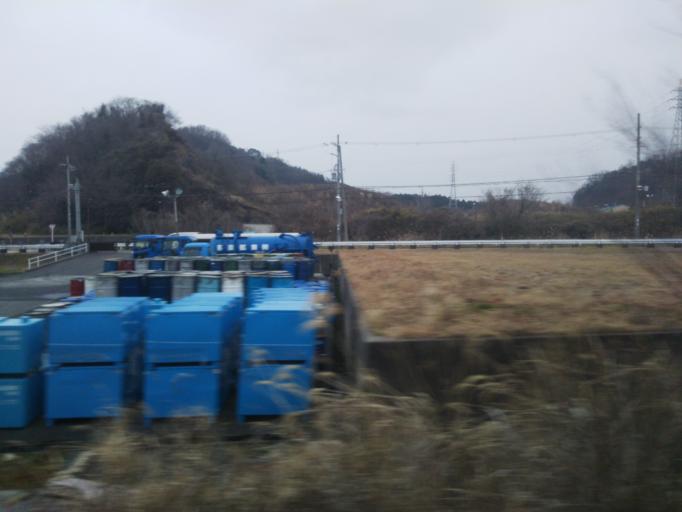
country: JP
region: Shiga Prefecture
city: Moriyama
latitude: 35.0210
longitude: 136.0474
